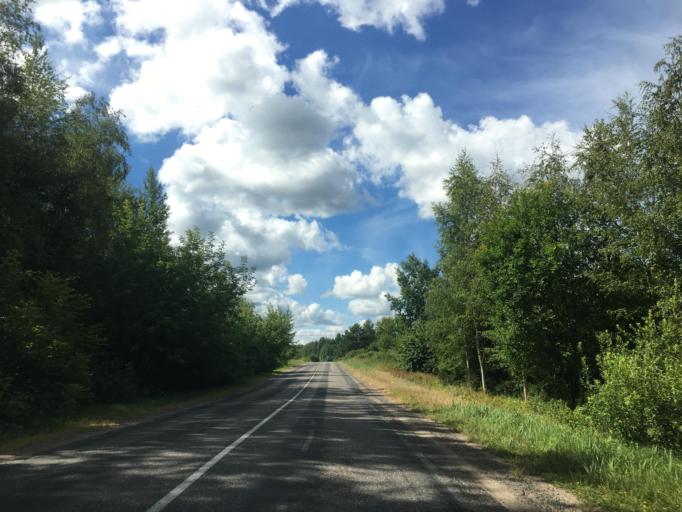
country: RU
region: Pskov
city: Pskov
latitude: 57.6905
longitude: 28.1749
